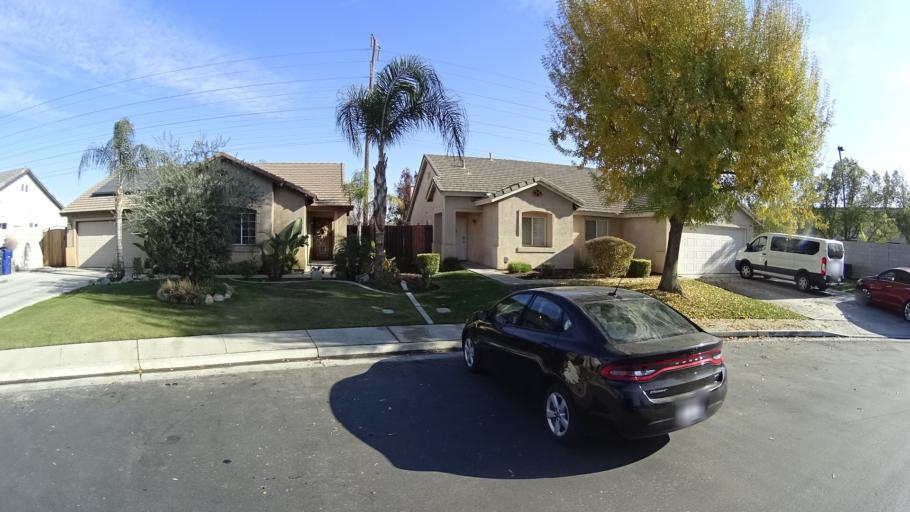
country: US
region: California
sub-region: Kern County
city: Greenacres
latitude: 35.3968
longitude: -119.0931
